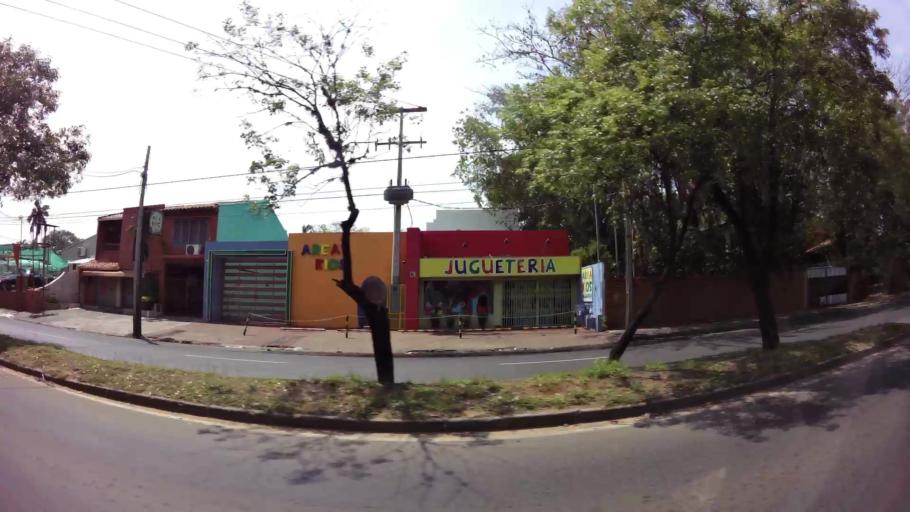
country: PY
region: Asuncion
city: Asuncion
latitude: -25.2829
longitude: -57.5876
